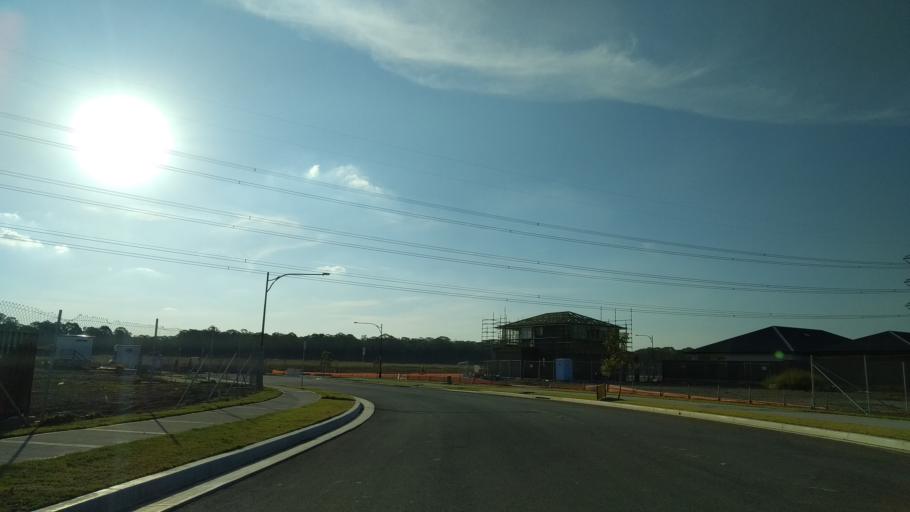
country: AU
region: New South Wales
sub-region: Penrith Municipality
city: Werrington County
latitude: -33.7302
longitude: 150.7554
